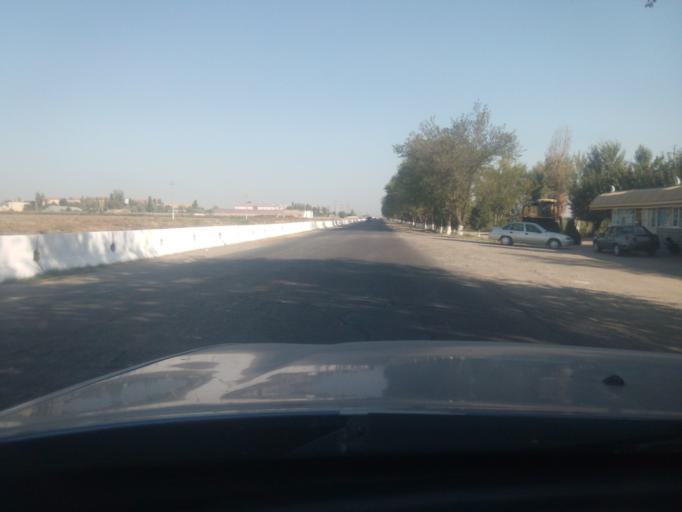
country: UZ
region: Sirdaryo
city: Guliston
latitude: 40.5111
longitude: 68.7952
